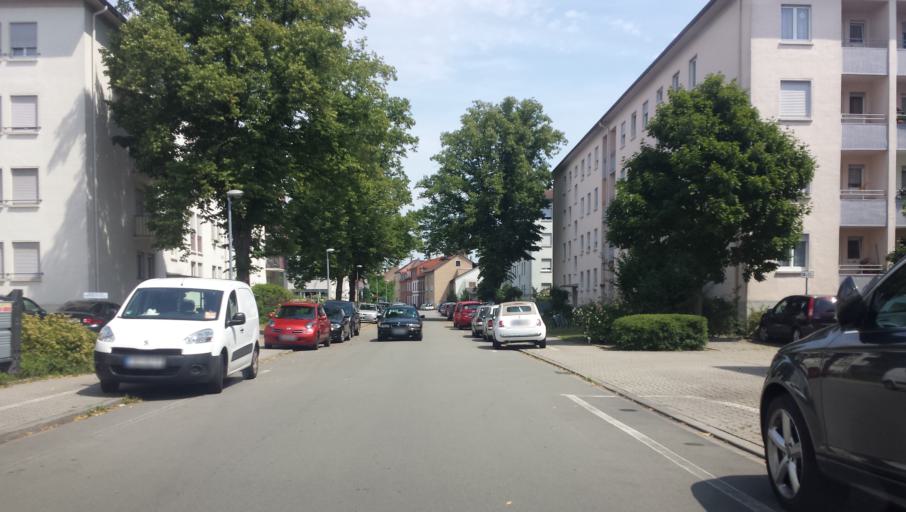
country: DE
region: Rheinland-Pfalz
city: Speyer
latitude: 49.3111
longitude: 8.4251
